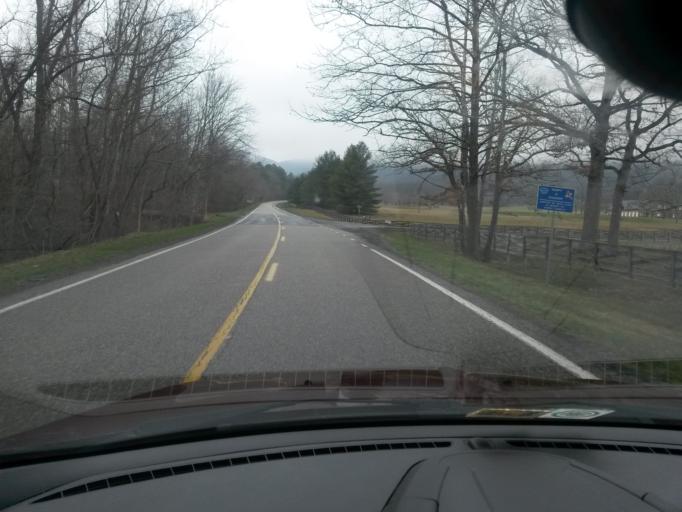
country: US
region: Virginia
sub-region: Bath County
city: Warm Springs
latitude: 38.0506
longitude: -79.7219
